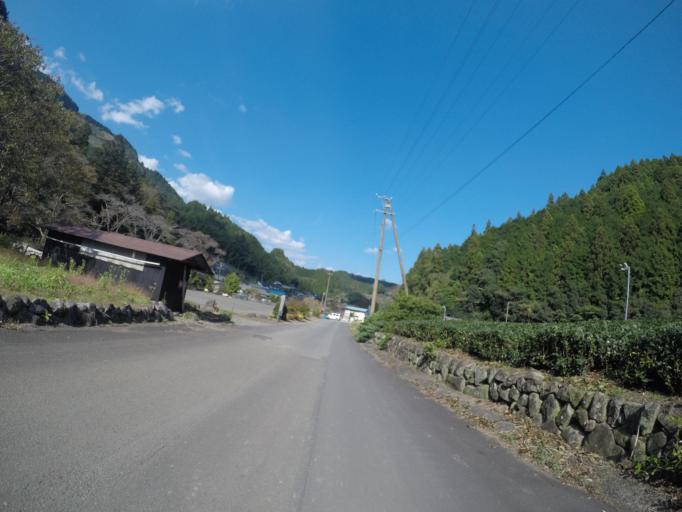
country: JP
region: Shizuoka
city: Shizuoka-shi
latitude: 35.1060
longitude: 138.4491
